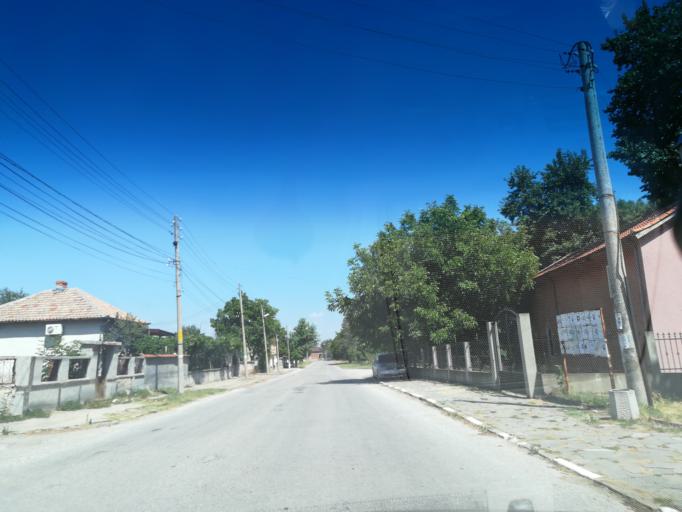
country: BG
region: Plovdiv
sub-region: Obshtina Sadovo
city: Sadovo
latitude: 42.0118
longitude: 25.0517
